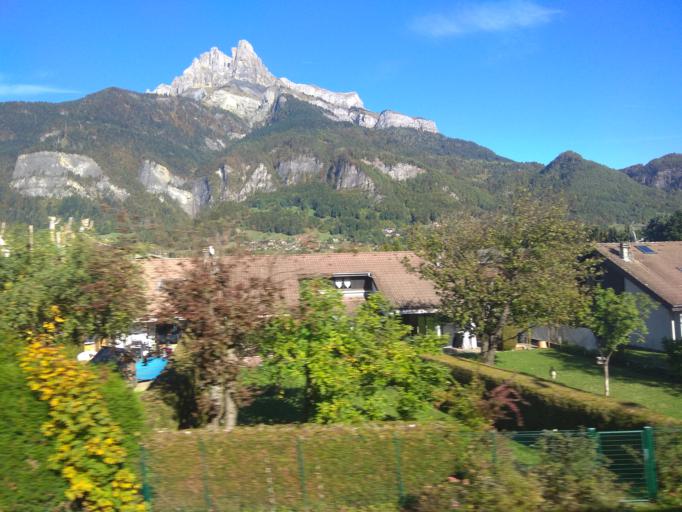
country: FR
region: Rhone-Alpes
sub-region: Departement de la Haute-Savoie
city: Sallanches
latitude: 45.9307
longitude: 6.6382
